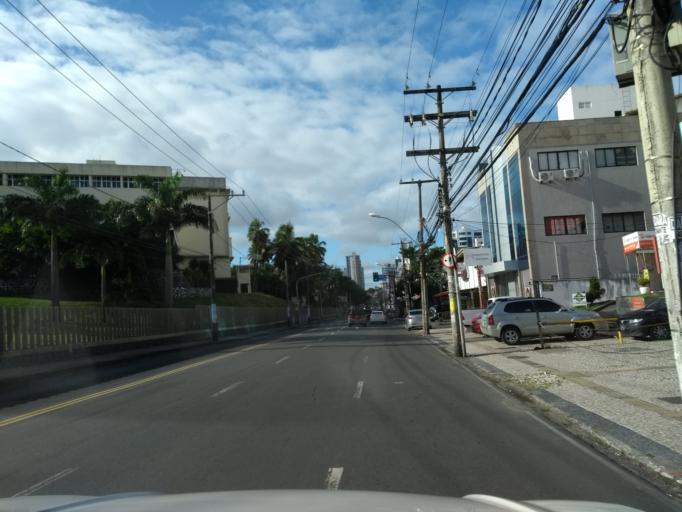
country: BR
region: Bahia
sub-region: Salvador
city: Salvador
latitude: -12.9978
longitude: -38.4547
